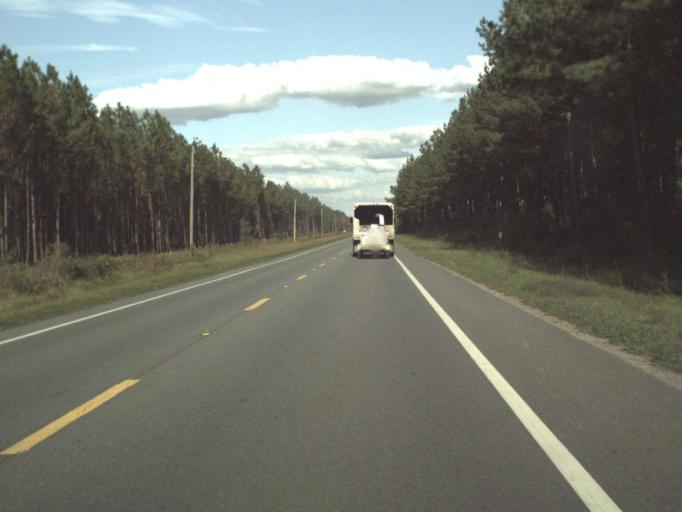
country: US
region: Florida
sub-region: Holmes County
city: Bonifay
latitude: 30.6513
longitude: -85.6737
